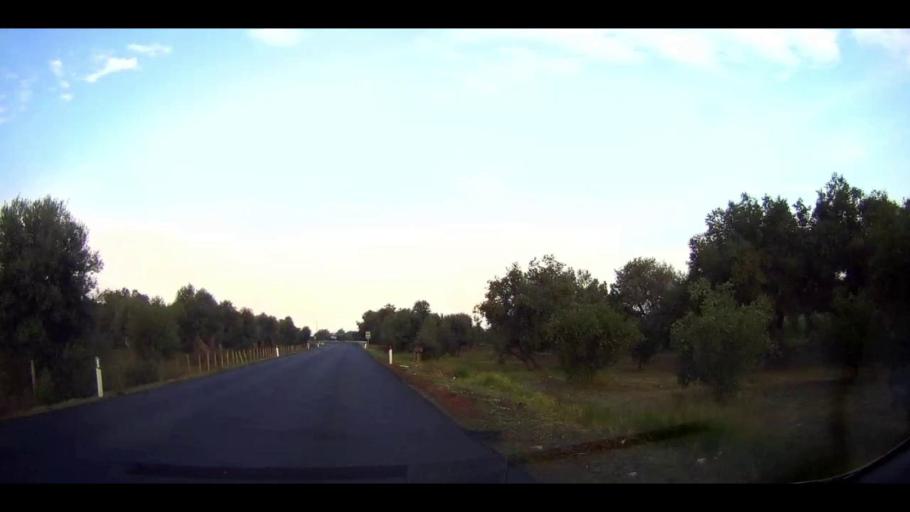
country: IT
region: Calabria
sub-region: Provincia di Crotone
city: Torretta
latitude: 39.4696
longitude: 17.0192
